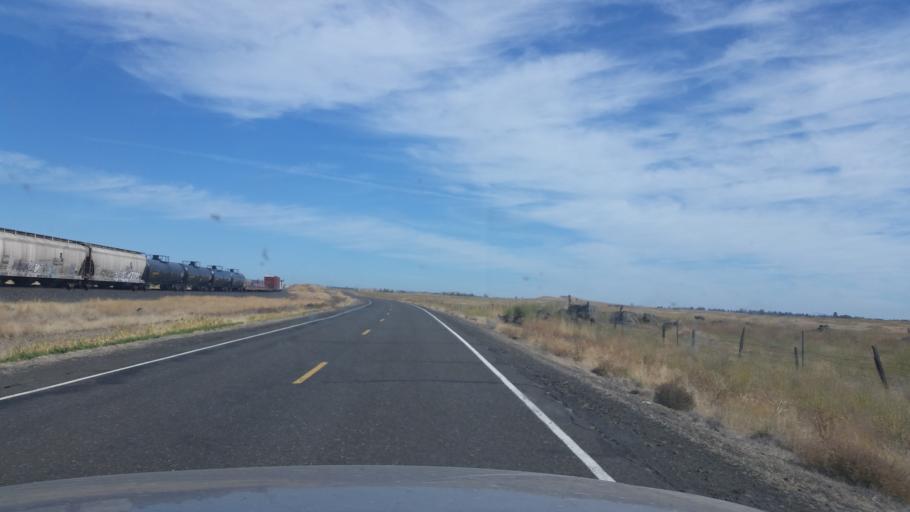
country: US
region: Washington
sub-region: Spokane County
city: Medical Lake
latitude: 47.3105
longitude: -117.9100
